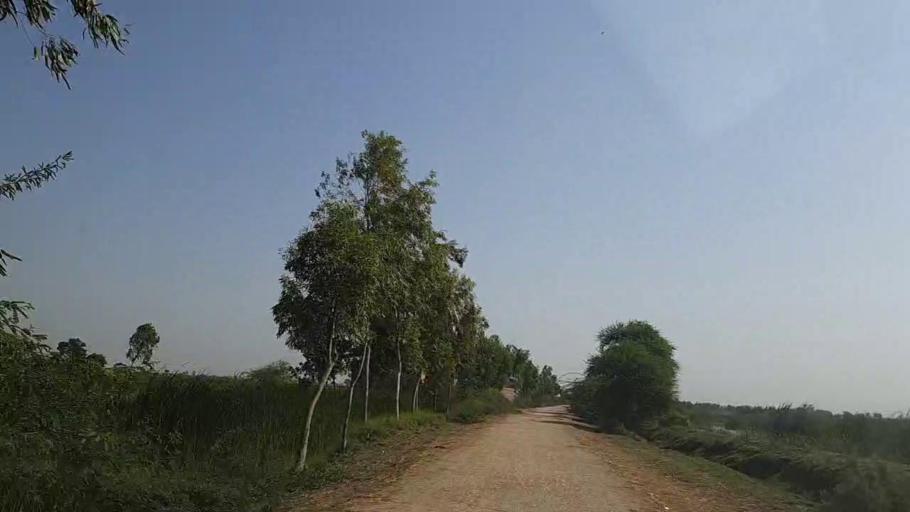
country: PK
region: Sindh
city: Daro Mehar
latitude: 24.7210
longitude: 68.0992
